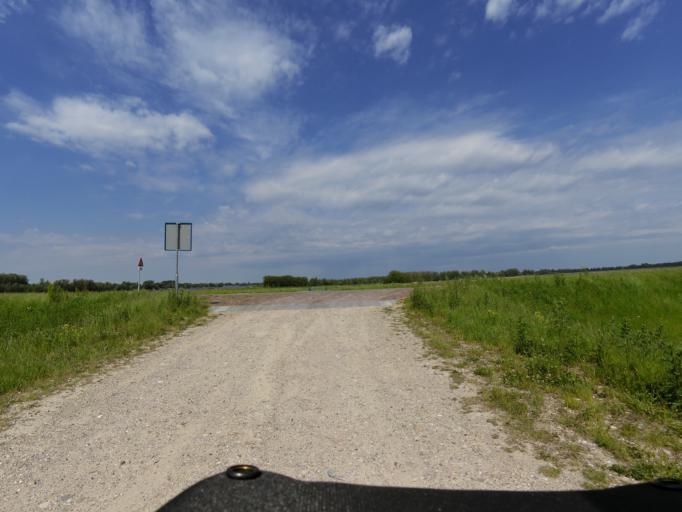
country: NL
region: North Brabant
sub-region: Gemeente Woudrichem
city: Woudrichem
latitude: 51.8006
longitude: 5.0476
